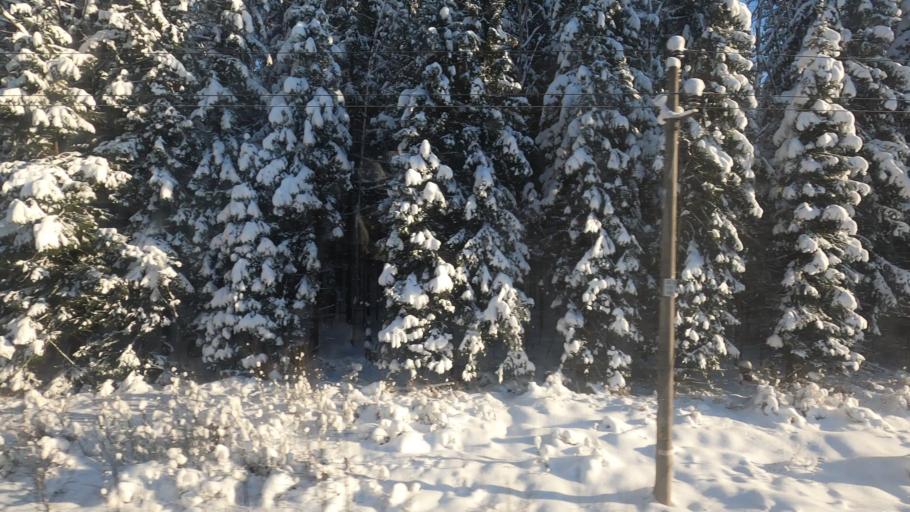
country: RU
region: Moskovskaya
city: Verbilki
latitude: 56.5265
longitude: 37.5587
